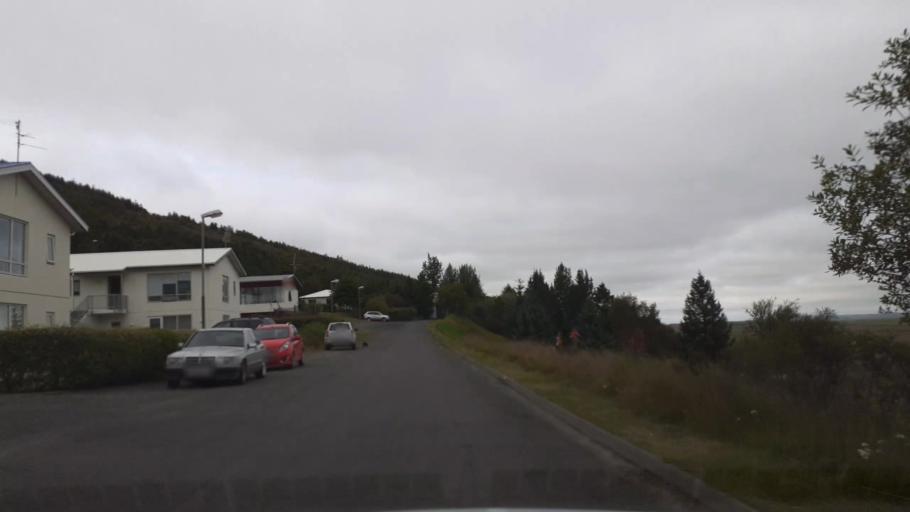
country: IS
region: Northwest
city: Saudarkrokur
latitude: 65.5544
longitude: -19.4494
